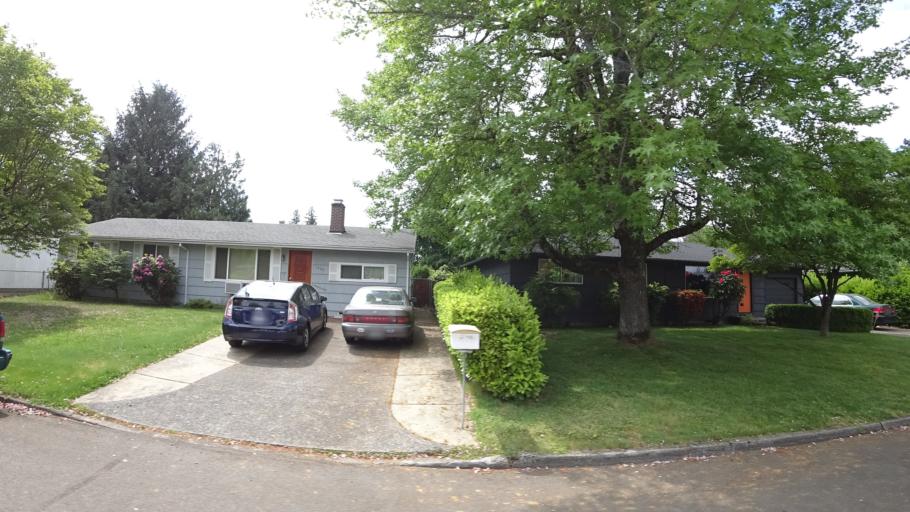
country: US
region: Oregon
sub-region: Multnomah County
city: Gresham
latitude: 45.5144
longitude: -122.4790
